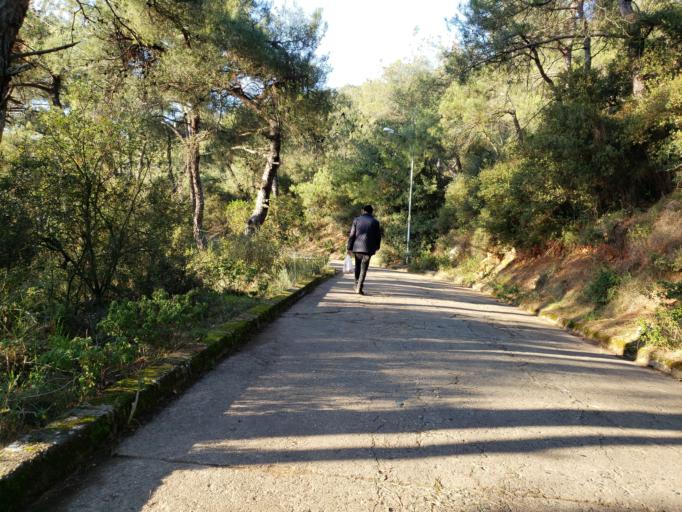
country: TR
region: Istanbul
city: Adalan
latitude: 40.8740
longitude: 29.0899
